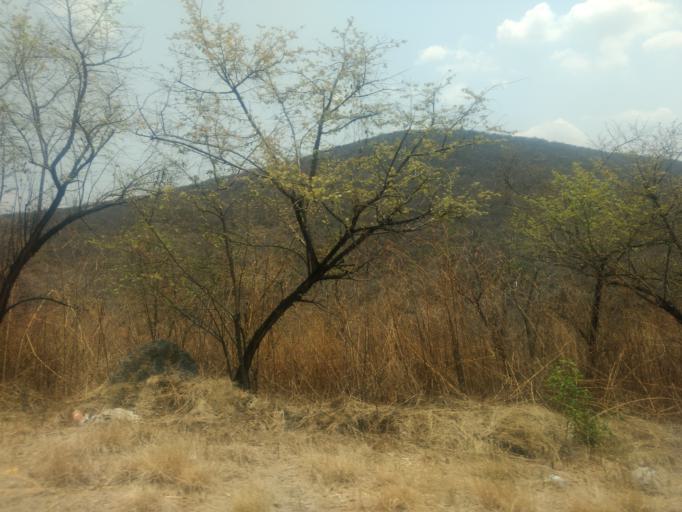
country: MX
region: Morelos
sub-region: Mazatepec
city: Cuauchichinola
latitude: 18.6541
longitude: -99.4057
